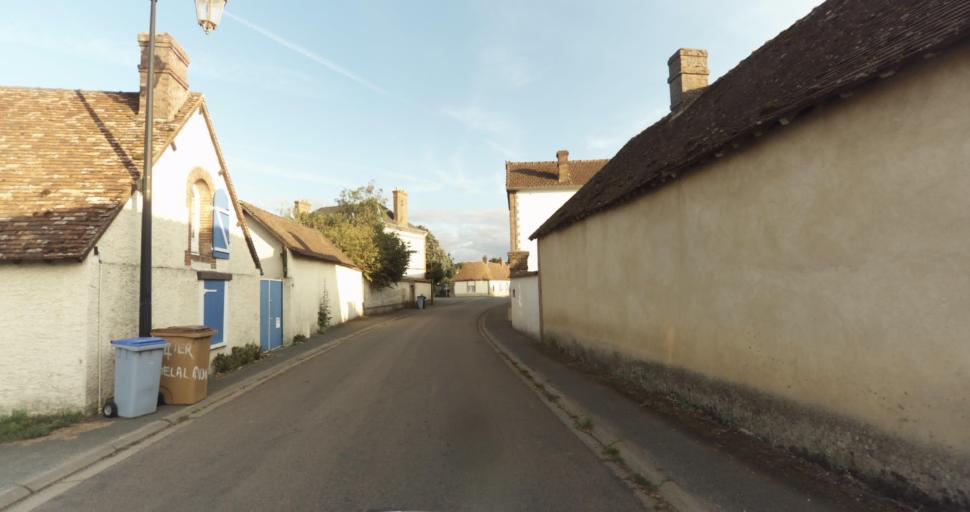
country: FR
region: Haute-Normandie
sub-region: Departement de l'Eure
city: Saint-Germain-sur-Avre
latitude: 48.8224
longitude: 1.2664
